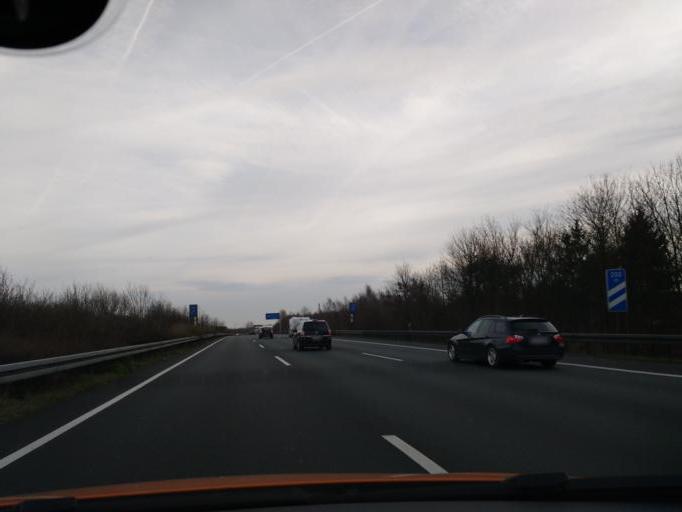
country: DE
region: Lower Saxony
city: Lehrte
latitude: 52.3832
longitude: 10.0174
